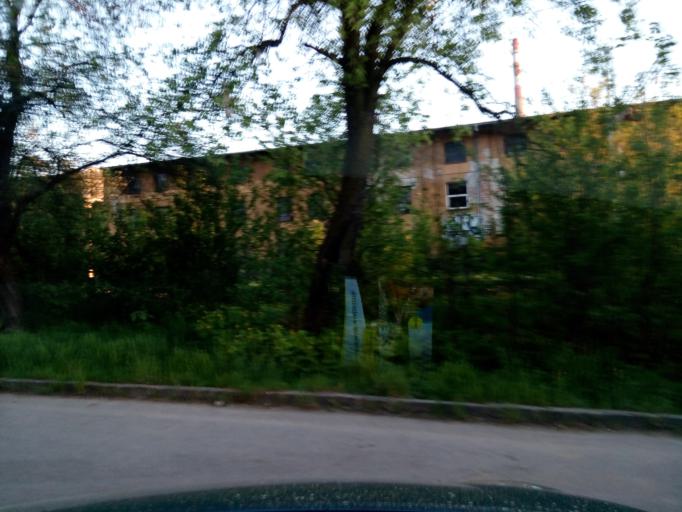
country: SK
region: Zilinsky
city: Ruzomberok
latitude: 49.0872
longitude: 19.2789
